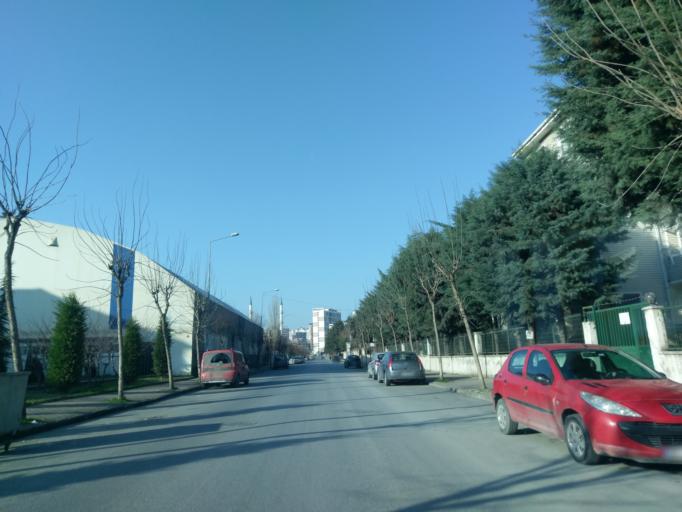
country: TR
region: Istanbul
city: Mahmutbey
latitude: 41.0311
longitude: 28.7660
